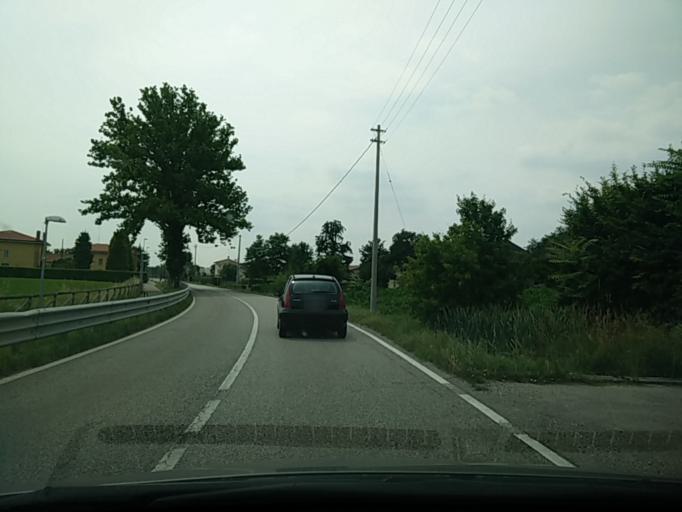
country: IT
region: Veneto
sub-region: Provincia di Treviso
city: Roncade
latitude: 45.6346
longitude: 12.3917
